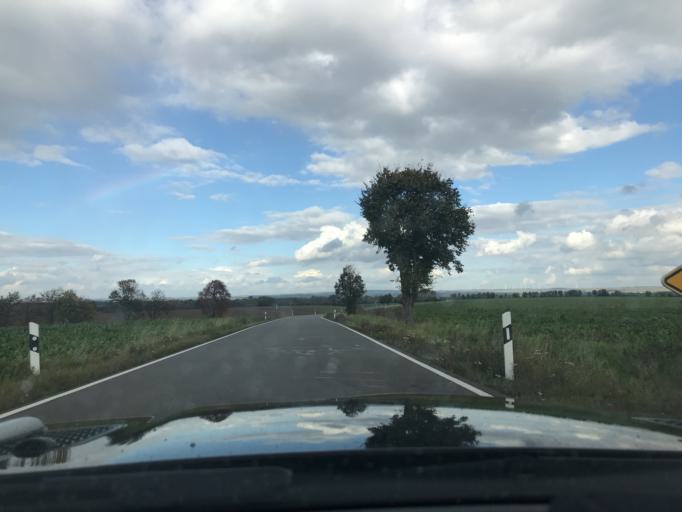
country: DE
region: Thuringia
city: Heroldishausen
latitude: 51.1293
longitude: 10.5172
